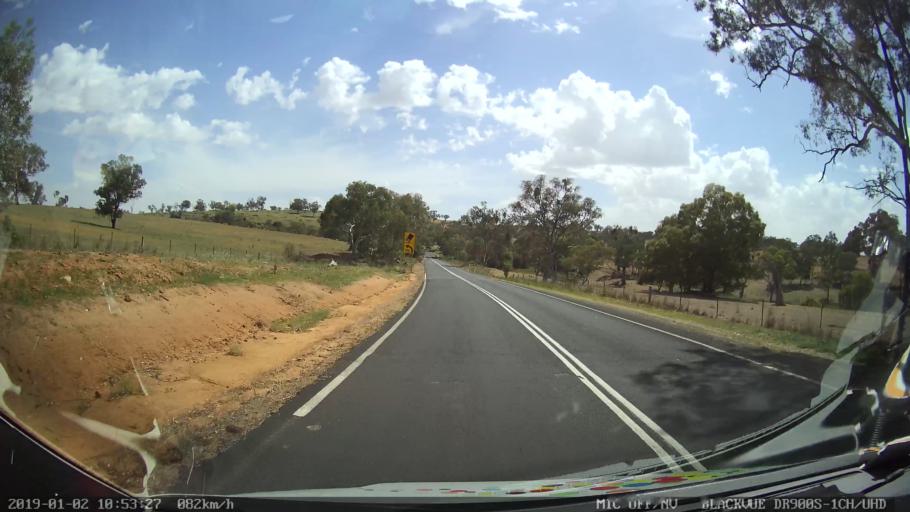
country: AU
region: New South Wales
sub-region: Cootamundra
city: Cootamundra
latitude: -34.6782
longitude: 148.2762
